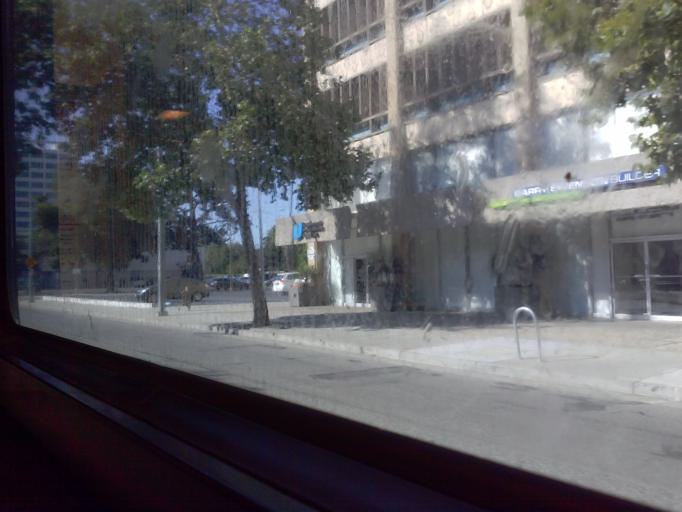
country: US
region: California
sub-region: Santa Clara County
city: San Jose
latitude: 37.3508
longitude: -121.9016
